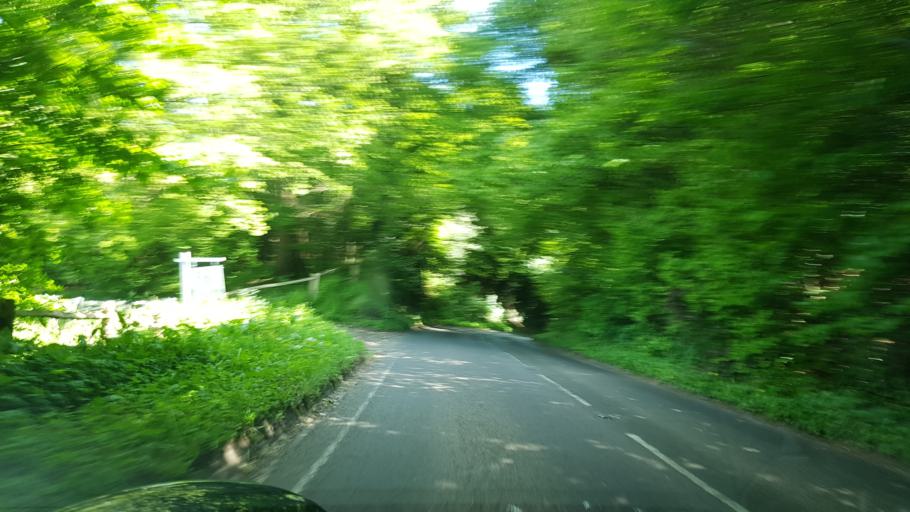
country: GB
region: England
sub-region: Surrey
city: Bramley
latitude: 51.1563
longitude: -0.5771
